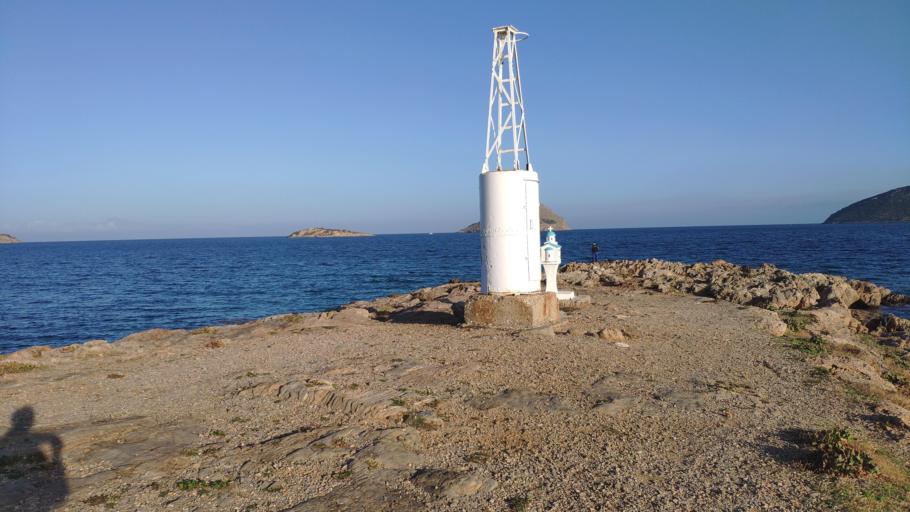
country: GR
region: Attica
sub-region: Nomarchia Anatolikis Attikis
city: Limin Mesoyaias
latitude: 37.8844
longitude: 24.0215
